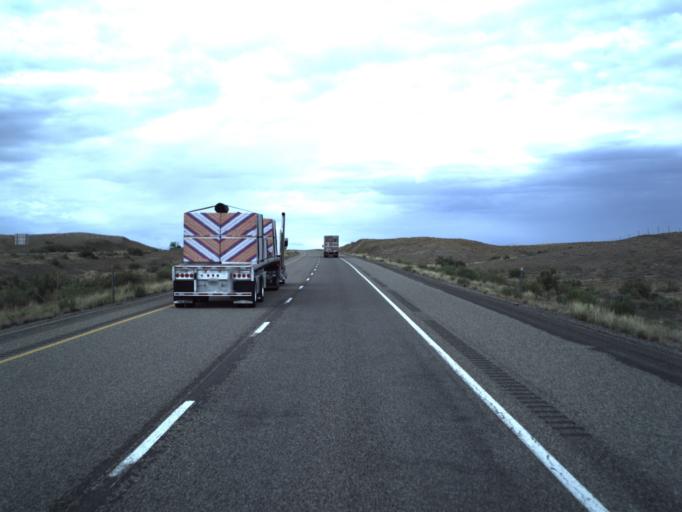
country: US
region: Colorado
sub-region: Mesa County
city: Loma
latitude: 39.1258
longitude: -109.1666
